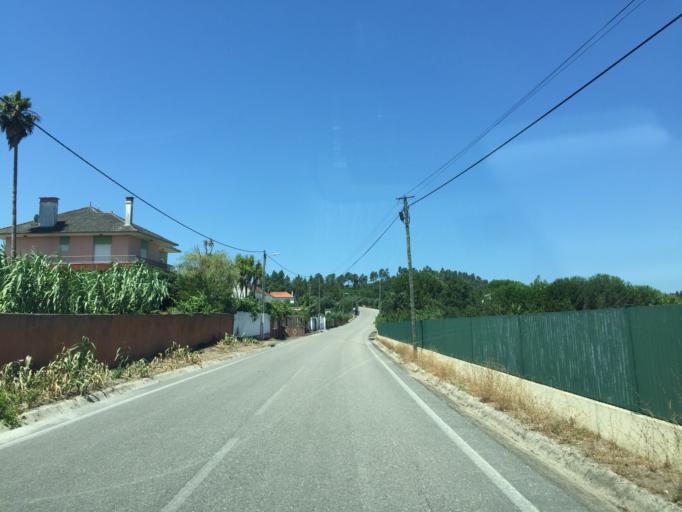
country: PT
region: Santarem
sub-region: Ferreira do Zezere
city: Ferreira do Zezere
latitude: 39.5954
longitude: -8.2837
